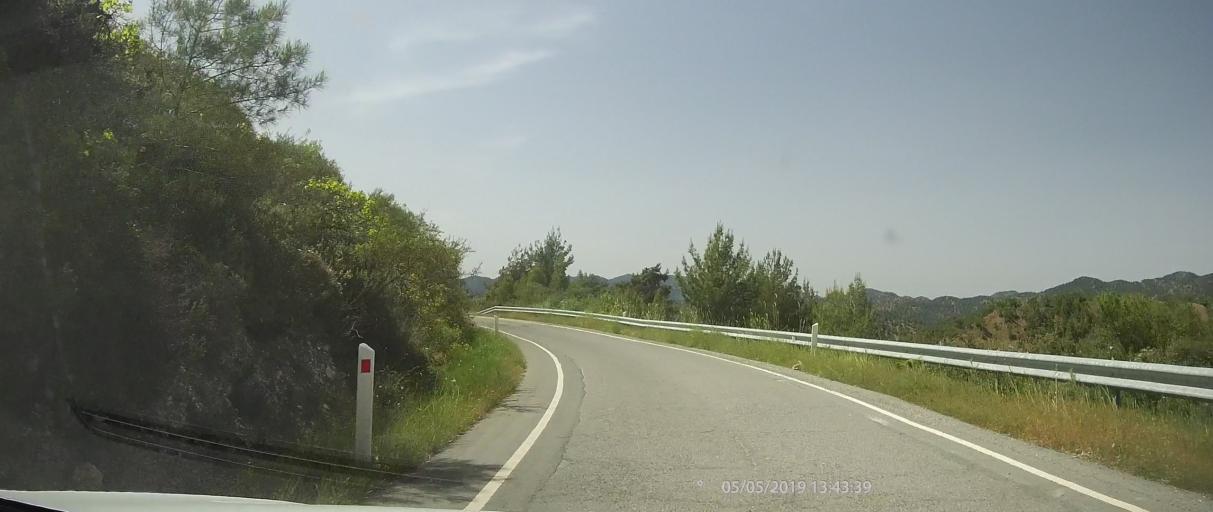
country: CY
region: Limassol
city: Pachna
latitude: 34.8742
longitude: 32.7949
